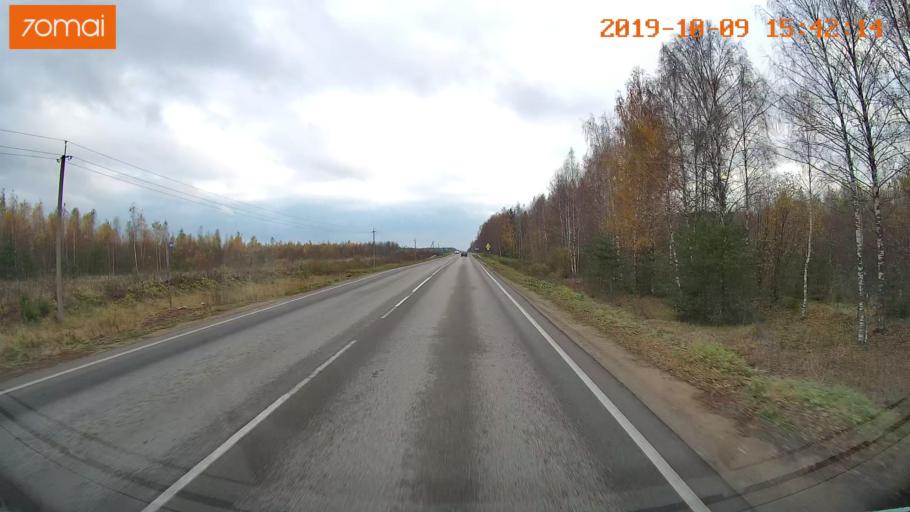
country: RU
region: Kostroma
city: Oktyabr'skiy
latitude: 57.8705
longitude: 41.1105
